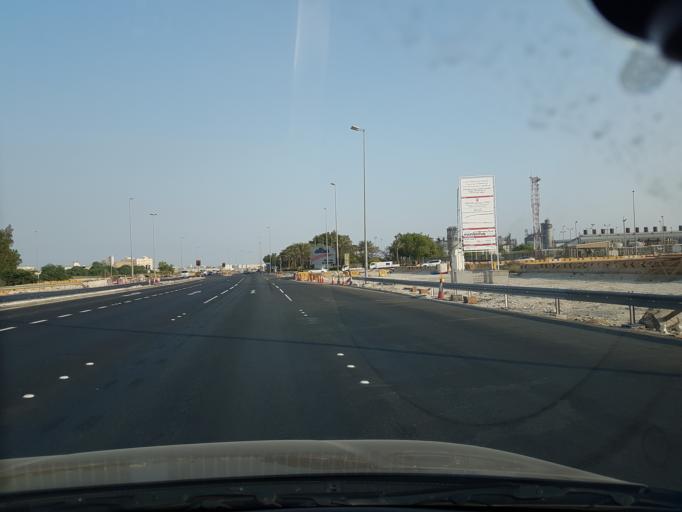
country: BH
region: Northern
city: Sitrah
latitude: 26.0990
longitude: 50.6052
